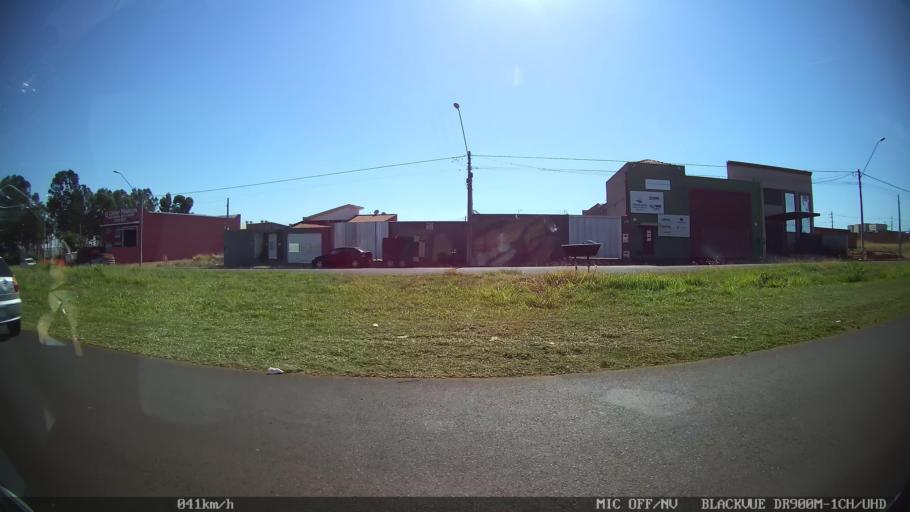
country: BR
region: Sao Paulo
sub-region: Batatais
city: Batatais
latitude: -20.8755
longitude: -47.5836
